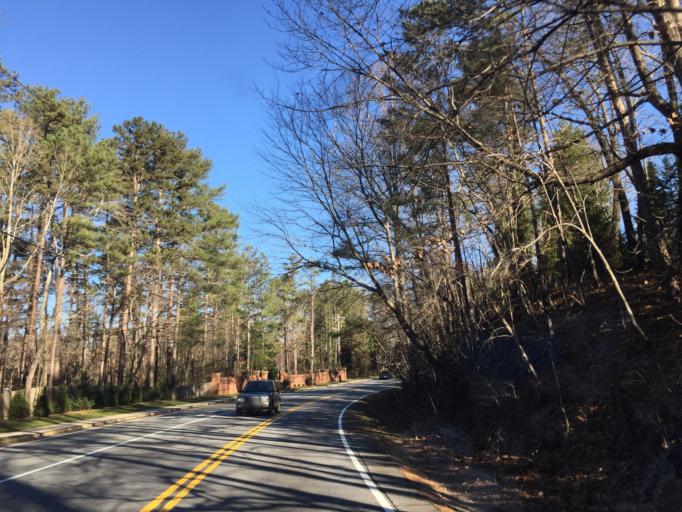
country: US
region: Georgia
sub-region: Fulton County
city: Johns Creek
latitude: 34.0128
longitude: -84.2521
